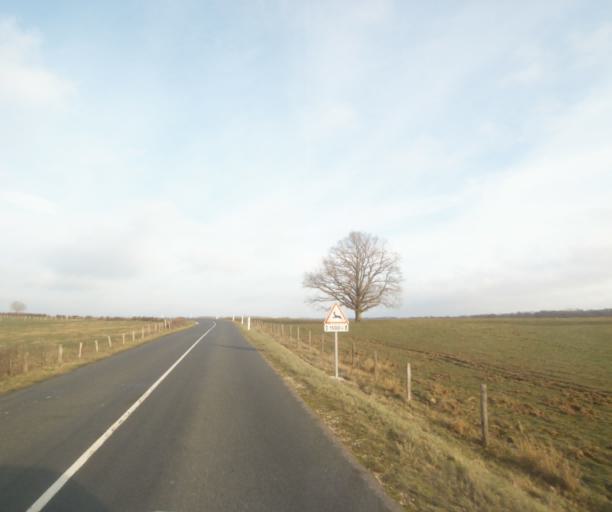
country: FR
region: Champagne-Ardenne
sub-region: Departement de la Marne
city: Sermaize-les-Bains
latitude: 48.7281
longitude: 4.9363
